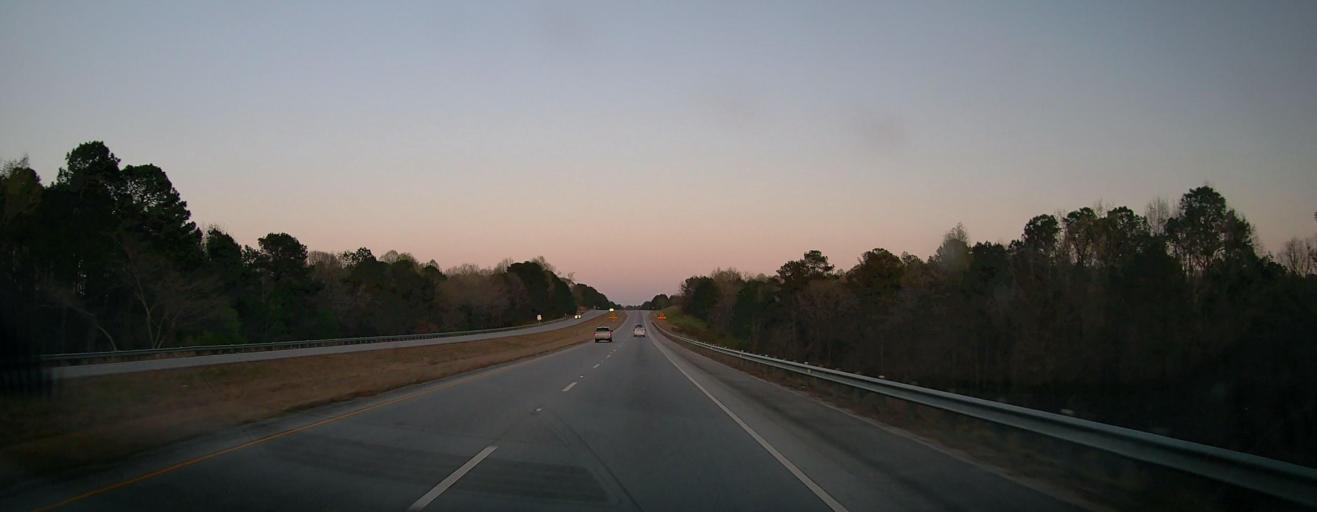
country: US
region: Alabama
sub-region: Tallapoosa County
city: Alexander City
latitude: 32.9065
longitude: -85.9146
